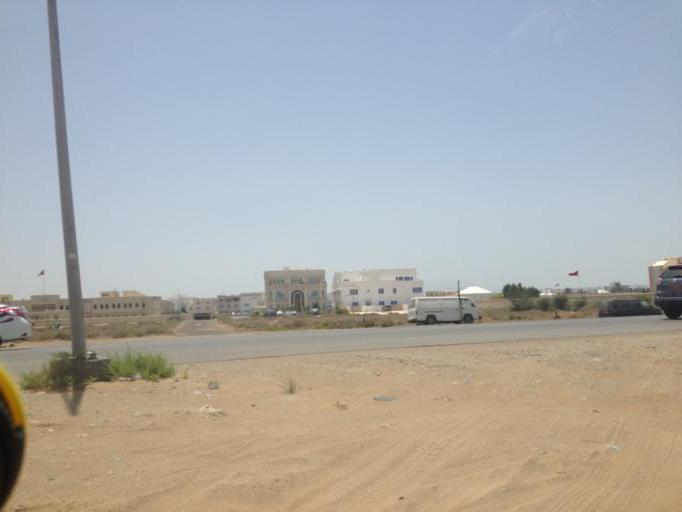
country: OM
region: Muhafazat Masqat
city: As Sib al Jadidah
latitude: 23.6298
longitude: 58.2535
